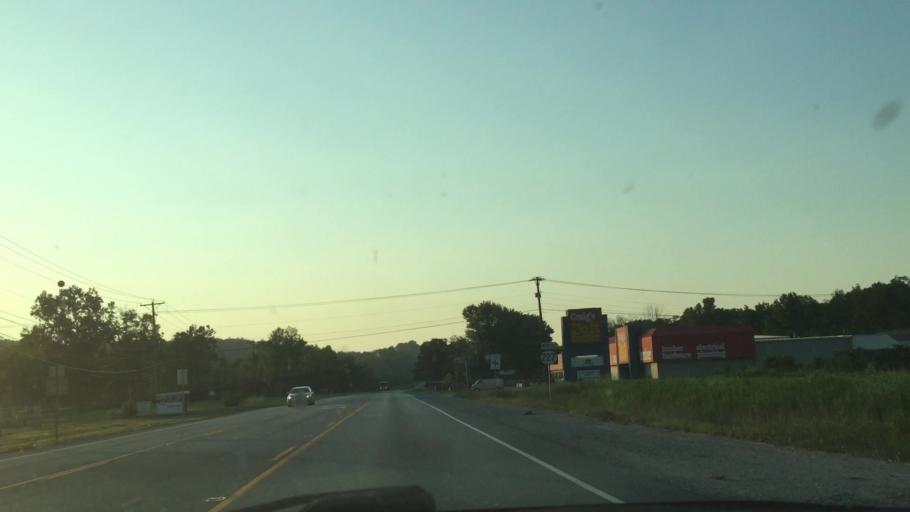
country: US
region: Kentucky
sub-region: Carroll County
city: Carrollton
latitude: 38.6651
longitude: -85.1414
